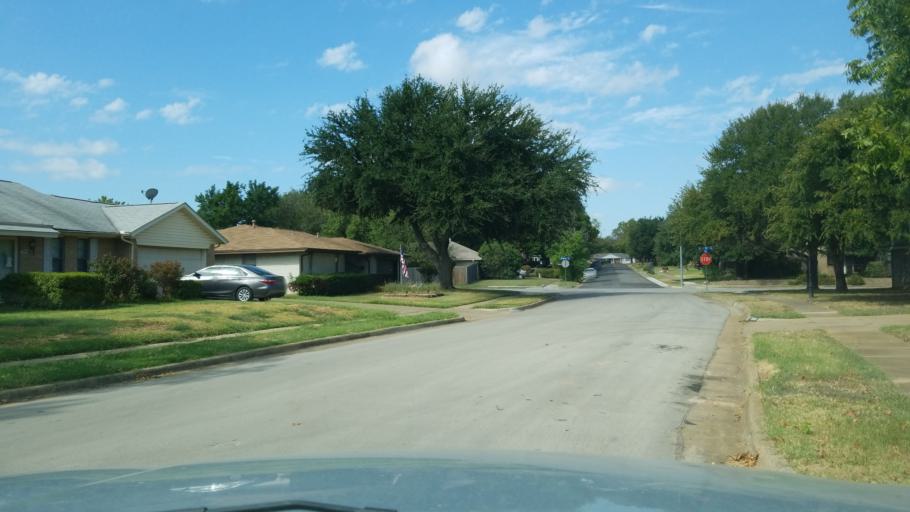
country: US
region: Texas
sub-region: Tarrant County
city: Euless
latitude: 32.8432
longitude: -97.0779
